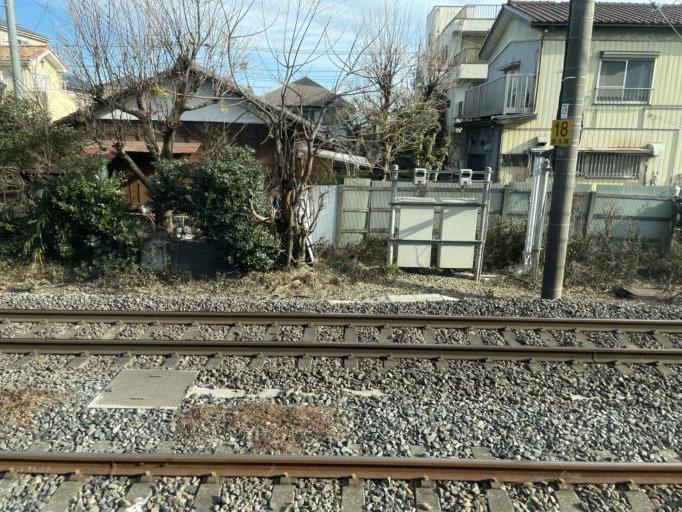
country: JP
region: Saitama
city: Okegawa
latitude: 36.0012
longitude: 139.5614
